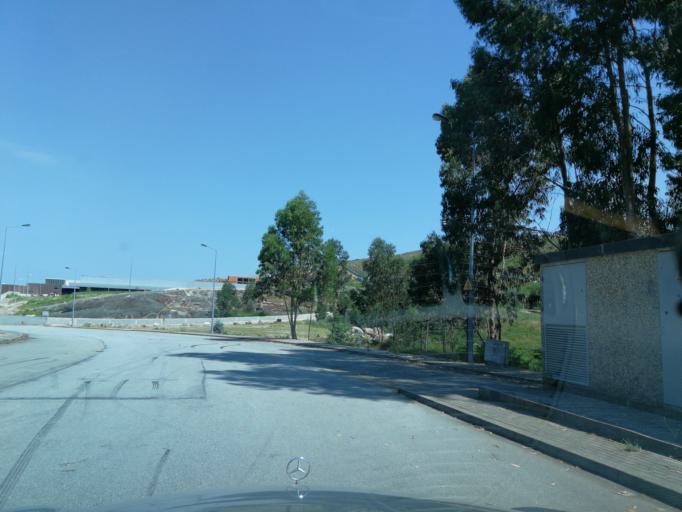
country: PT
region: Braga
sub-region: Braga
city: Adaufe
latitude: 41.5602
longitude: -8.3450
